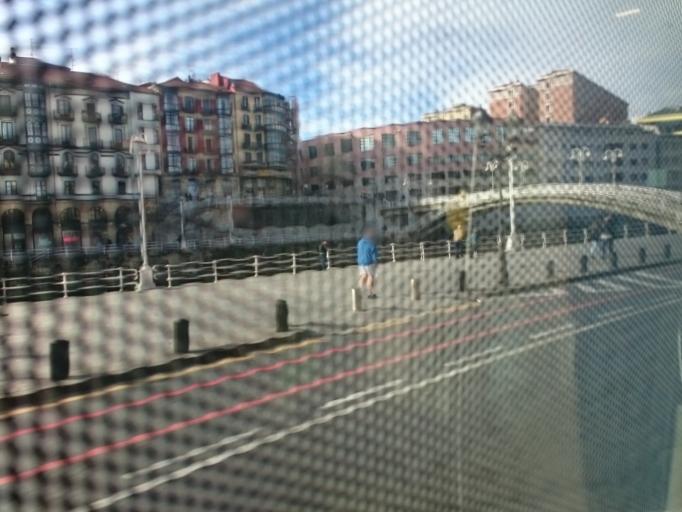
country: ES
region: Basque Country
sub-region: Bizkaia
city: Bilbao
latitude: 43.2560
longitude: -2.9250
